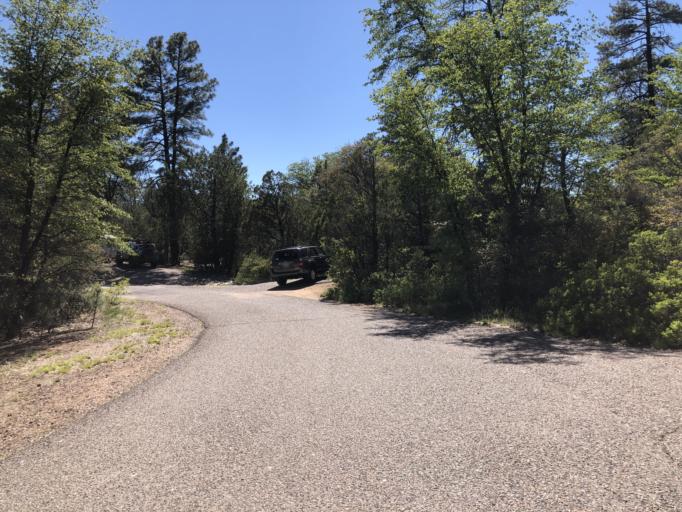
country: US
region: Arizona
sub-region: Gila County
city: Payson
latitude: 34.2712
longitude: -111.3208
